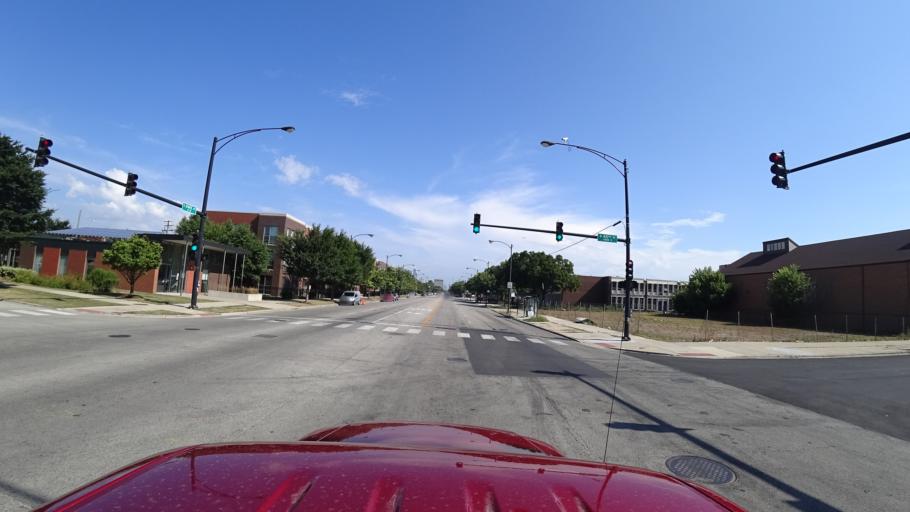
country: US
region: Illinois
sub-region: Cook County
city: Chicago
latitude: 41.8130
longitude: -87.6262
